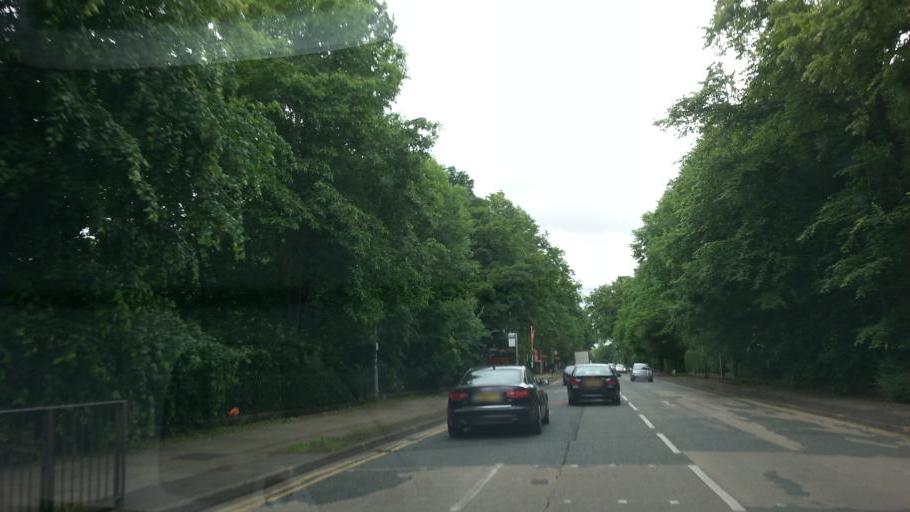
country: GB
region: England
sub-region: Borough of Bury
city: Prestwich
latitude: 53.5276
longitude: -2.2801
